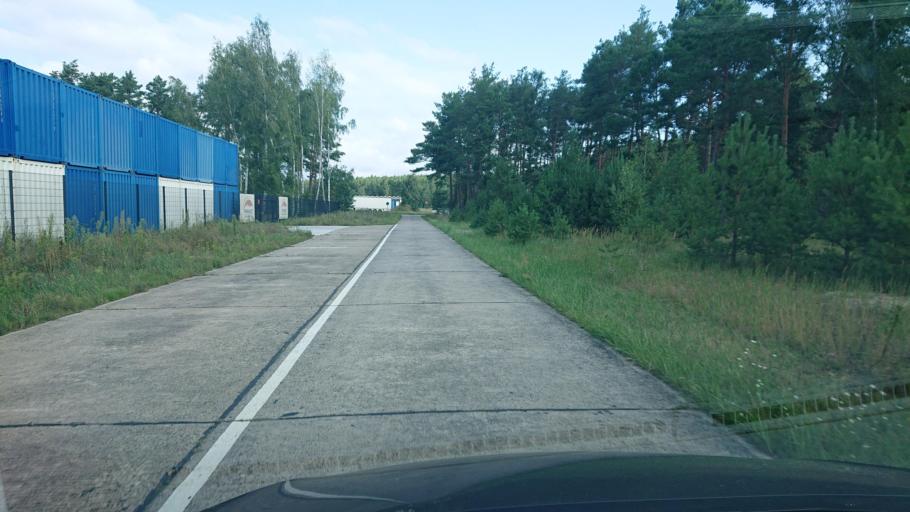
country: DE
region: Brandenburg
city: Gross Kreutz
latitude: 52.3574
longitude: 12.7784
